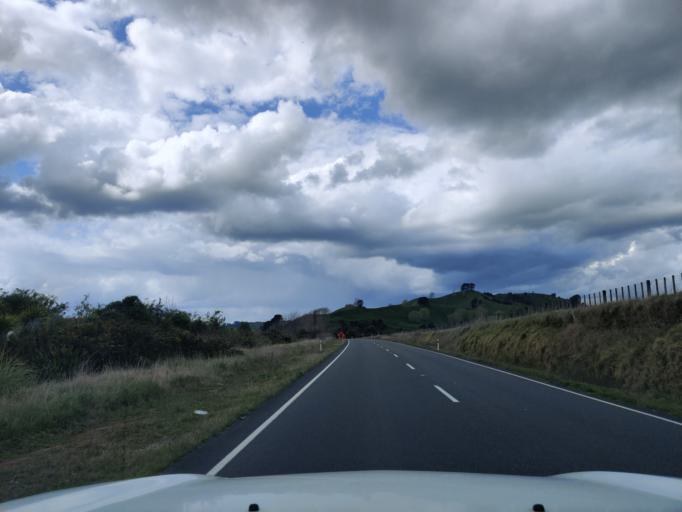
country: NZ
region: Manawatu-Wanganui
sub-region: Wanganui District
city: Wanganui
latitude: -39.8787
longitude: 175.1076
